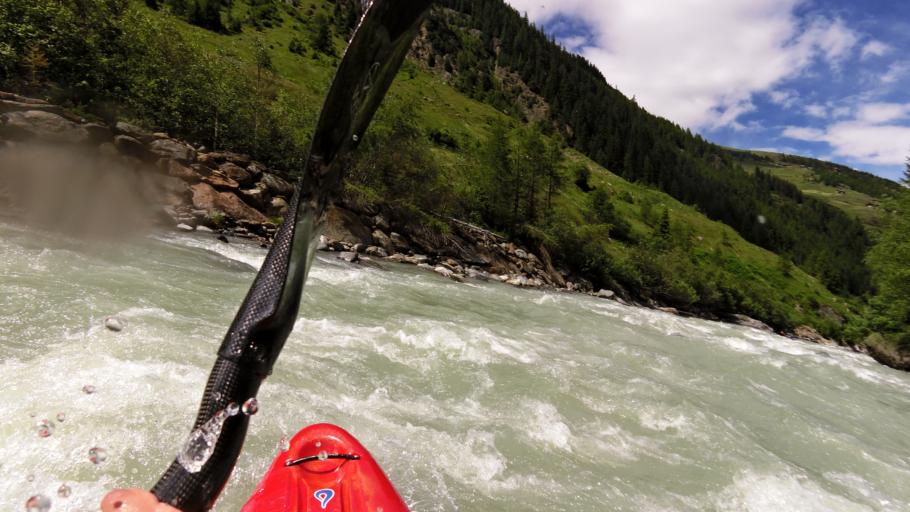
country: AT
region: Tyrol
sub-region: Politischer Bezirk Imst
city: Soelden
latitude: 46.9202
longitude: 10.9862
